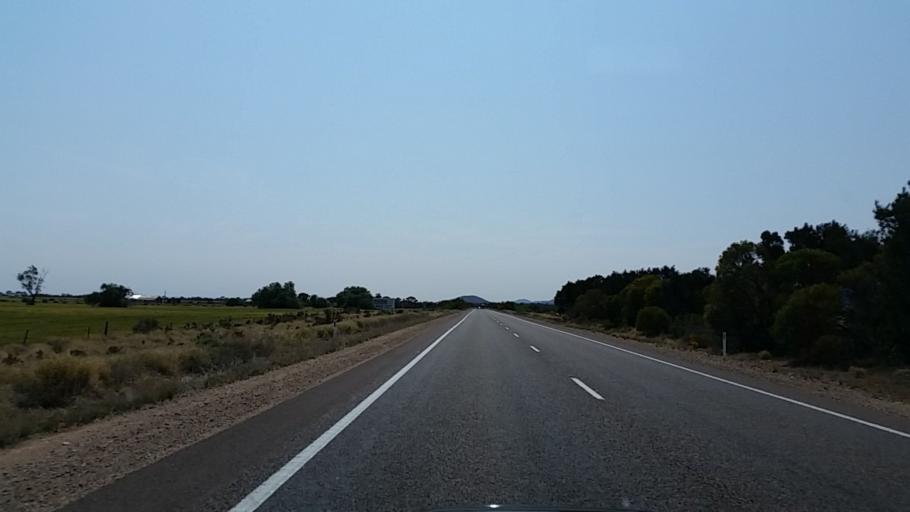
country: AU
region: South Australia
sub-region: Port Pirie City and Dists
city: Port Pirie
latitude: -32.8804
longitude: 137.9823
